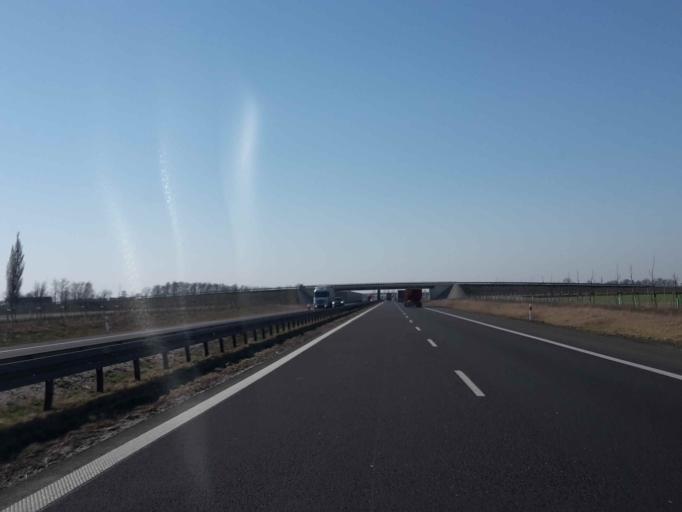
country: PL
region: Greater Poland Voivodeship
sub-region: Powiat poznanski
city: Kleszczewo
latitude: 52.3317
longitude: 17.1499
